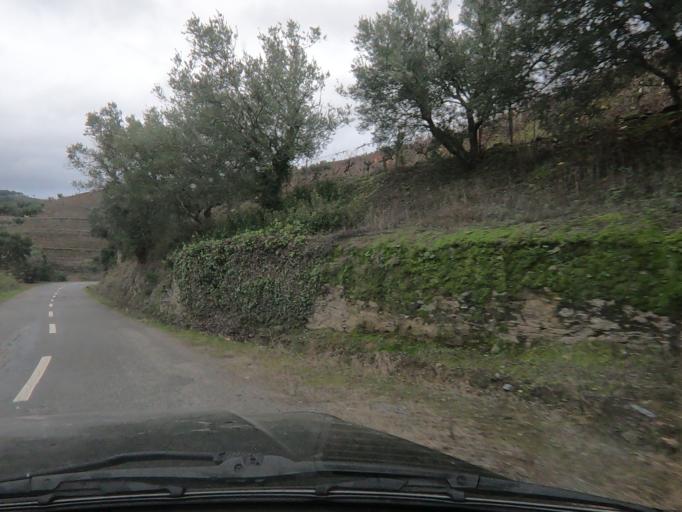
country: PT
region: Vila Real
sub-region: Santa Marta de Penaguiao
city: Santa Marta de Penaguiao
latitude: 41.2332
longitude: -7.7385
